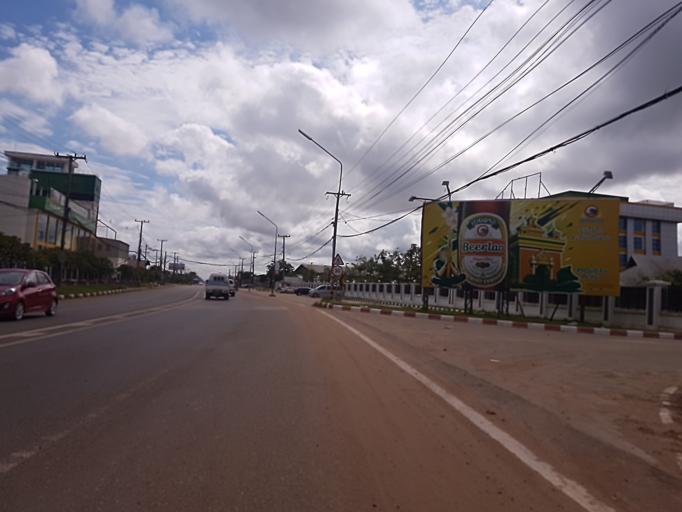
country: TH
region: Nong Khai
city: Tha Bo
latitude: 17.8705
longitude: 102.6553
